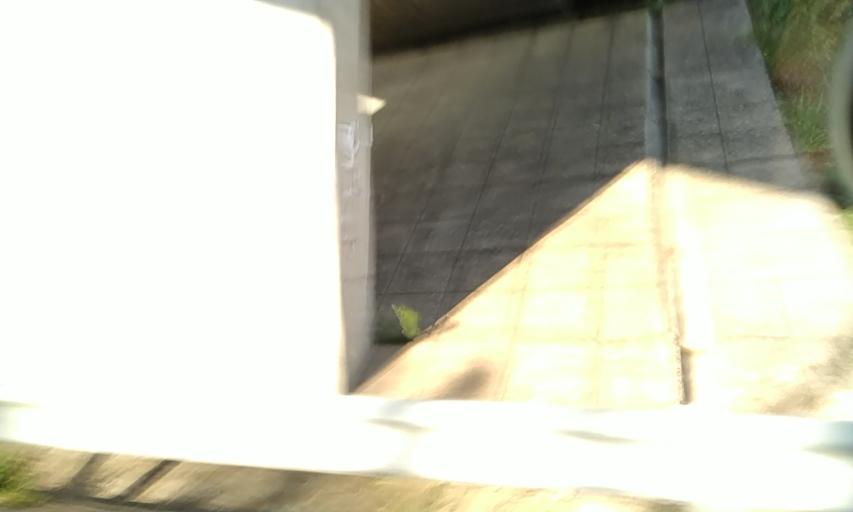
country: PT
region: Portalegre
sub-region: Portalegre
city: Portalegre
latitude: 39.3056
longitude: -7.4413
